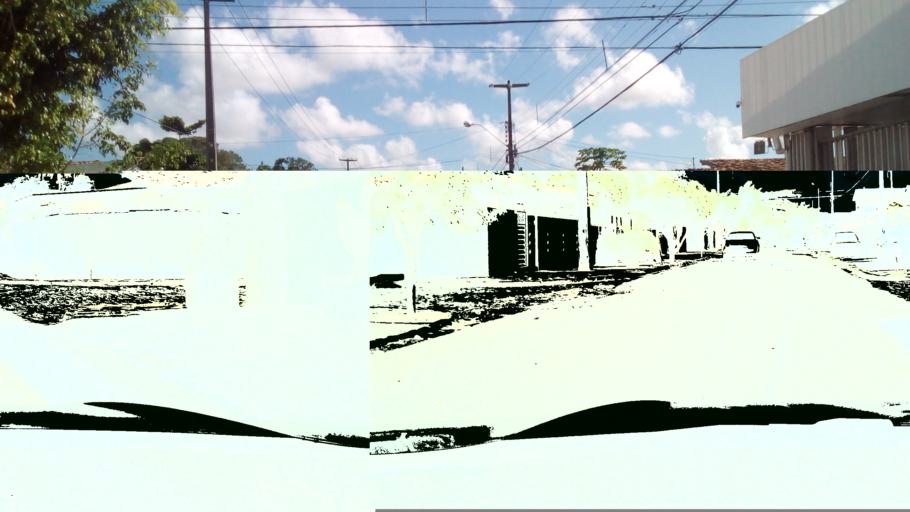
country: BR
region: Paraiba
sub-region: Joao Pessoa
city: Joao Pessoa
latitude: -7.1344
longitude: -34.8517
